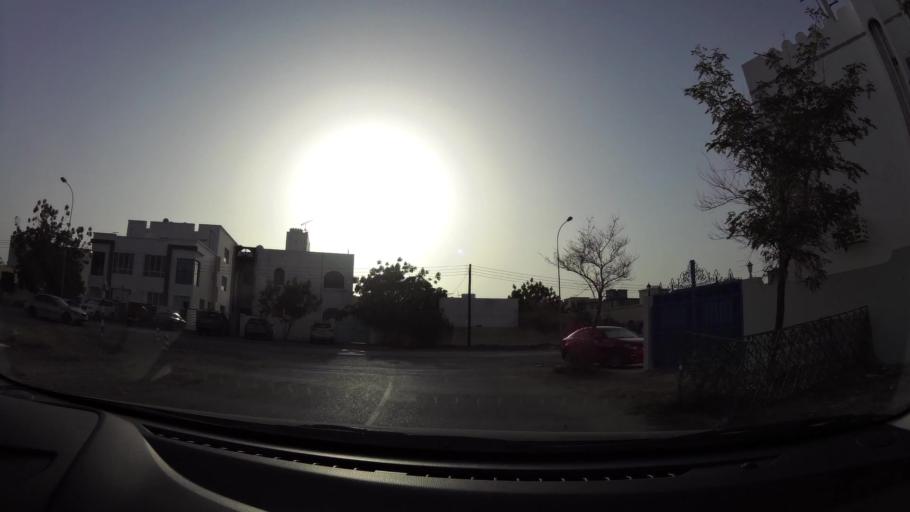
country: OM
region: Muhafazat Masqat
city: Bawshar
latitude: 23.5327
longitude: 58.3474
